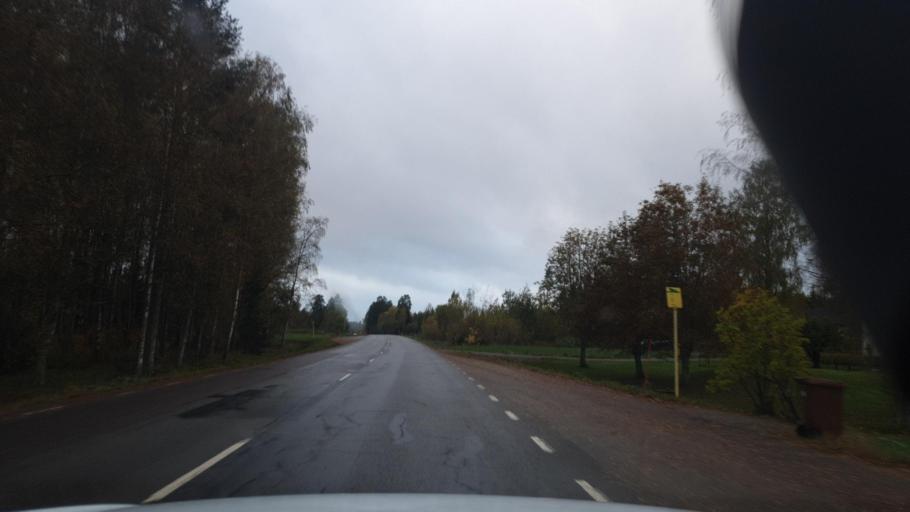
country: SE
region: Vaermland
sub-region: Arvika Kommun
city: Arvika
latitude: 59.6932
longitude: 12.6345
